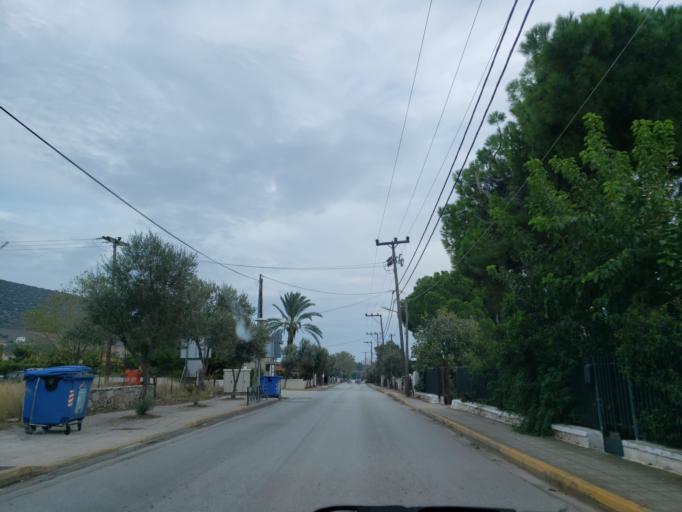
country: GR
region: Attica
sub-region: Nomarchia Anatolikis Attikis
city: Marathonas
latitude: 38.1527
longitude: 23.9624
